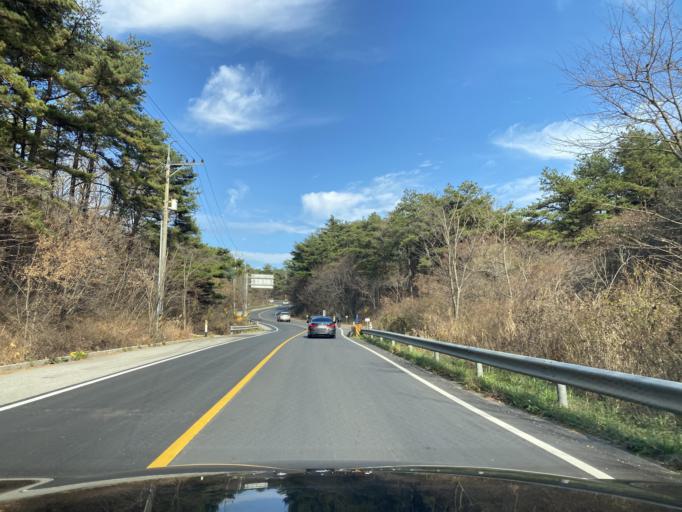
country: KR
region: Chungcheongnam-do
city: Hongsung
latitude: 36.6583
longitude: 126.6273
